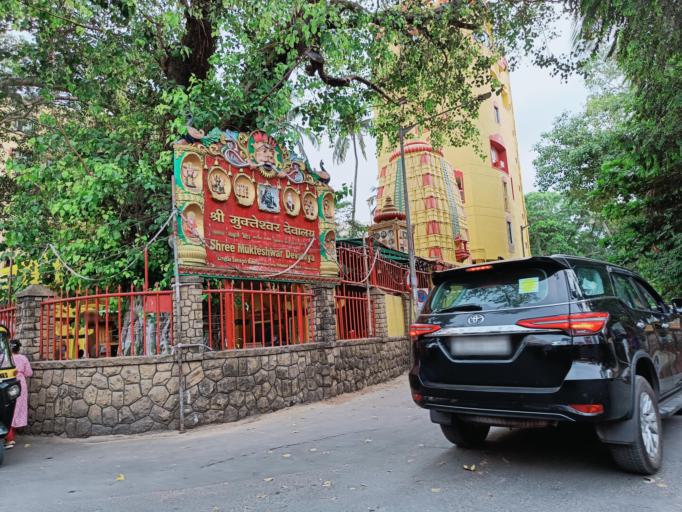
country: IN
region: Maharashtra
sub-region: Mumbai Suburban
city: Mumbai
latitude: 19.1141
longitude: 72.8260
